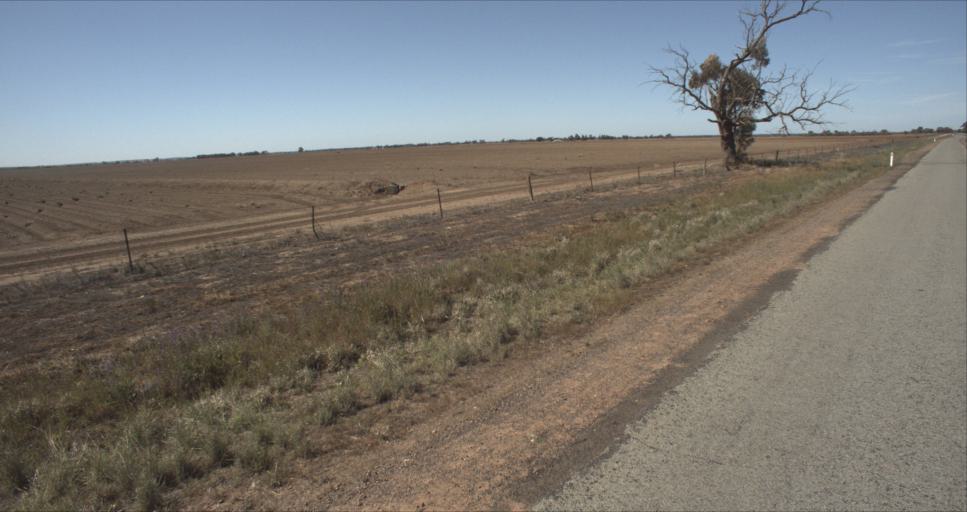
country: AU
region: New South Wales
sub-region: Leeton
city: Leeton
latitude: -34.5551
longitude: 146.3138
